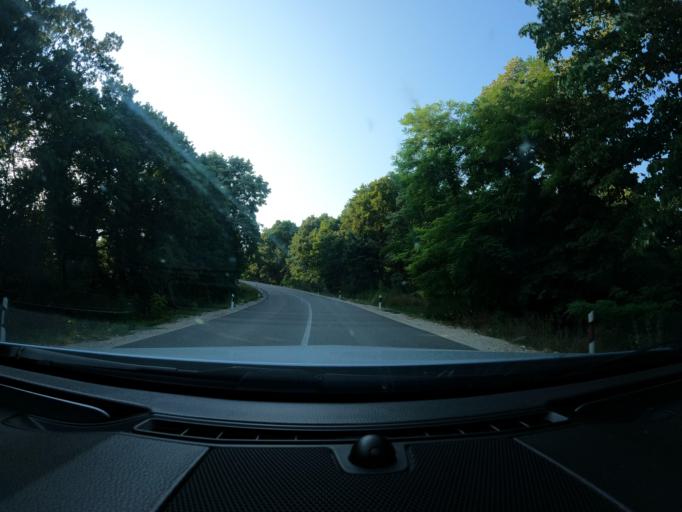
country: RS
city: Vrdnik
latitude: 45.1294
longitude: 19.7261
